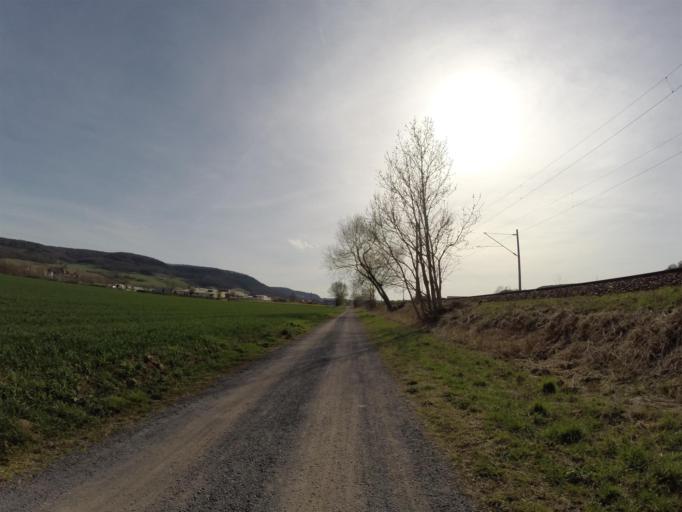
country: DE
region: Thuringia
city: Neuengonna
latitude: 50.9624
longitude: 11.6271
